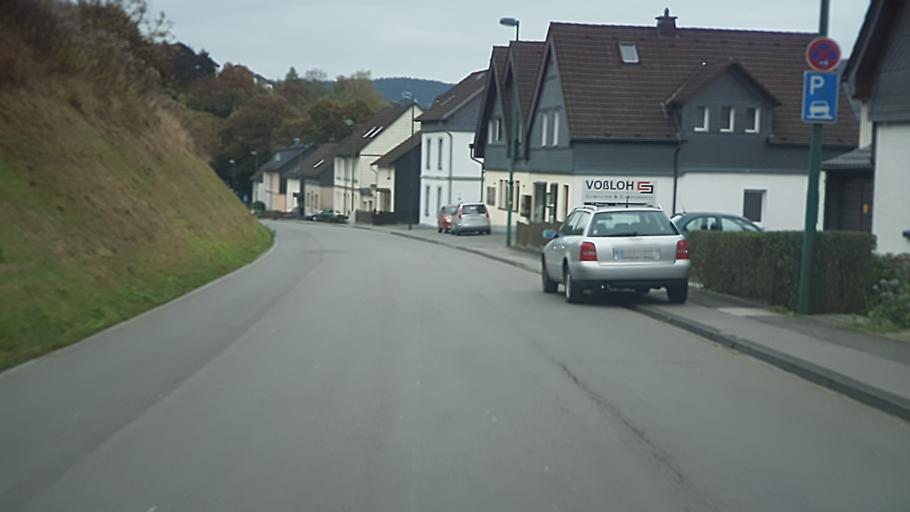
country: DE
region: North Rhine-Westphalia
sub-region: Regierungsbezirk Arnsberg
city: Attendorn
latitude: 51.1319
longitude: 7.8943
